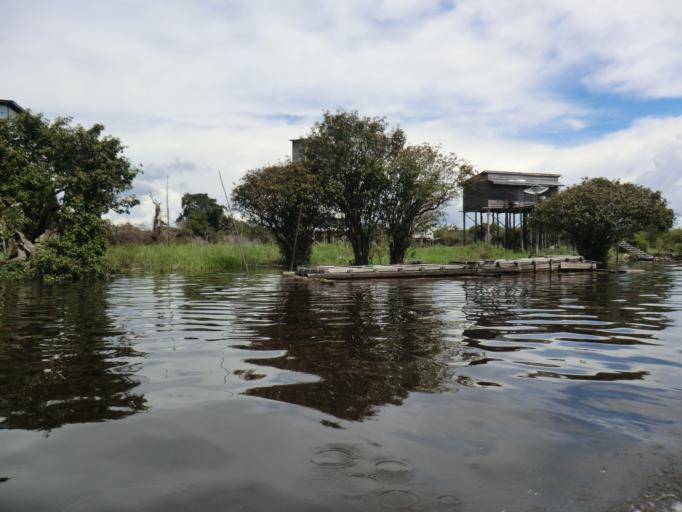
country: MY
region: Sarawak
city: Simanggang
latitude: 0.8460
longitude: 112.2374
